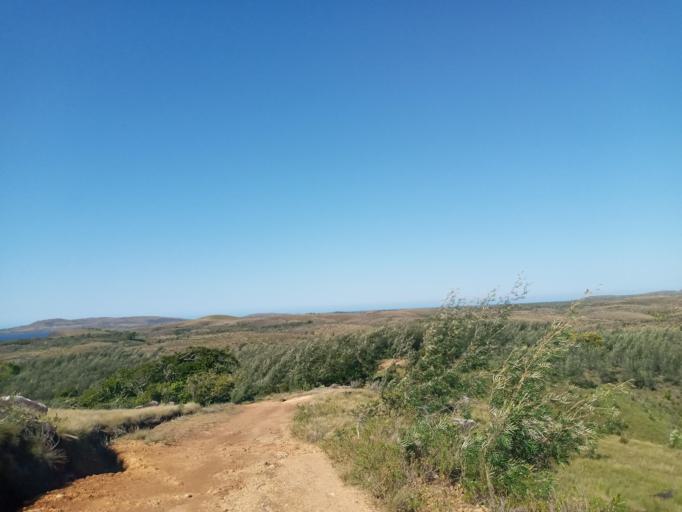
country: MG
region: Anosy
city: Fort Dauphin
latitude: -24.9129
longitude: 47.0828
